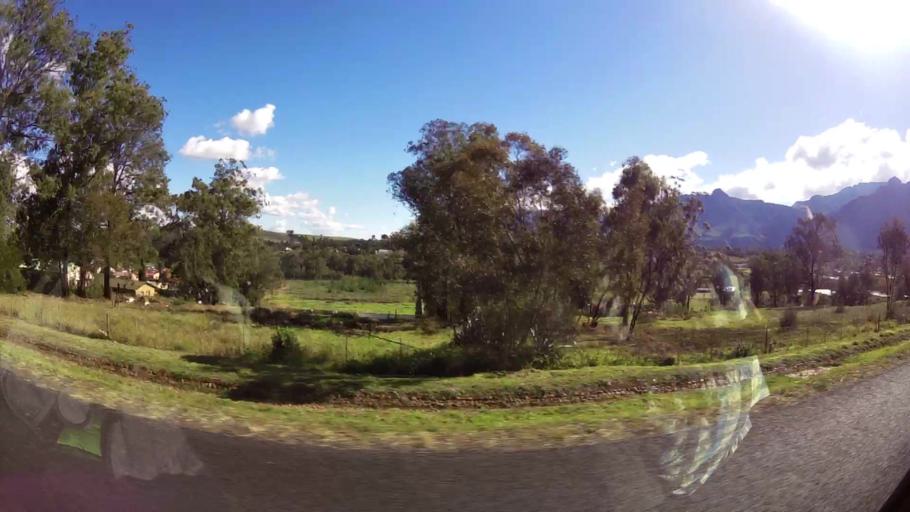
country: ZA
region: Western Cape
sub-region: Overberg District Municipality
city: Swellendam
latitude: -34.0377
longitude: 20.4337
